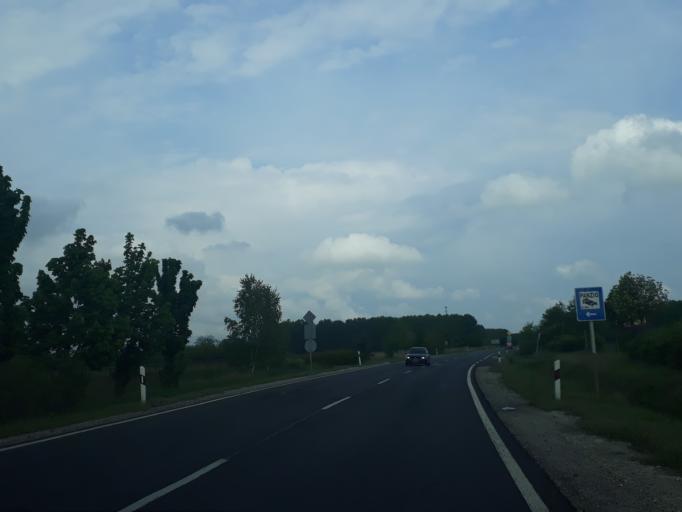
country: HU
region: Szabolcs-Szatmar-Bereg
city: Nyirbogdany
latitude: 48.0430
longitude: 21.8675
